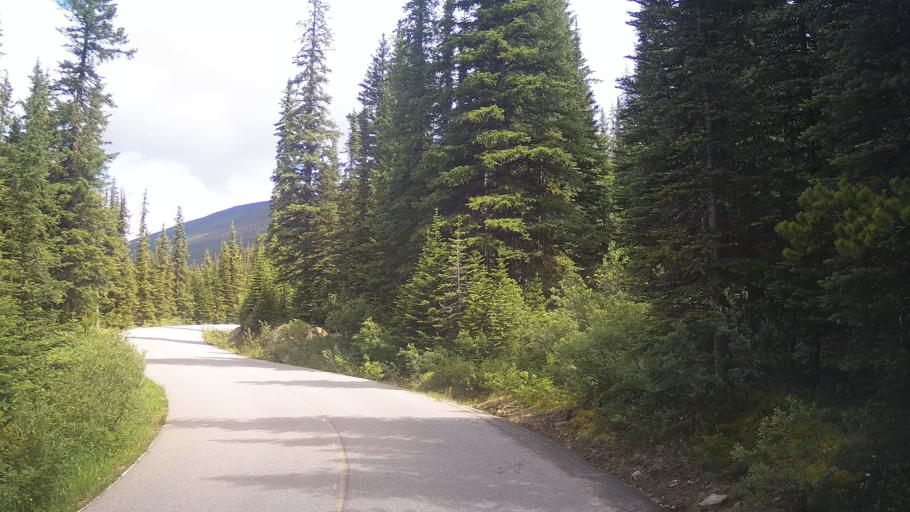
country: CA
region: Alberta
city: Jasper Park Lodge
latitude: 52.7044
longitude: -118.0601
